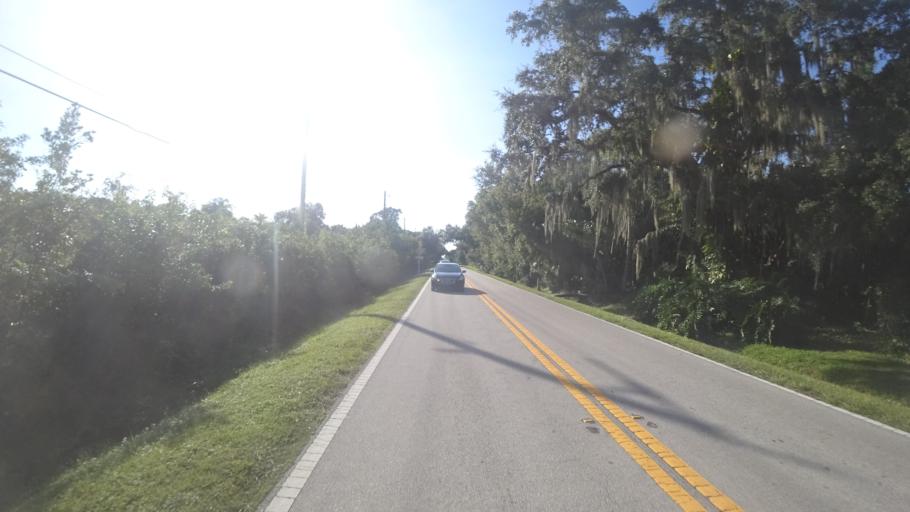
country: US
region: Florida
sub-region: Sarasota County
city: North Sarasota
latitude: 27.3817
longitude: -82.5225
